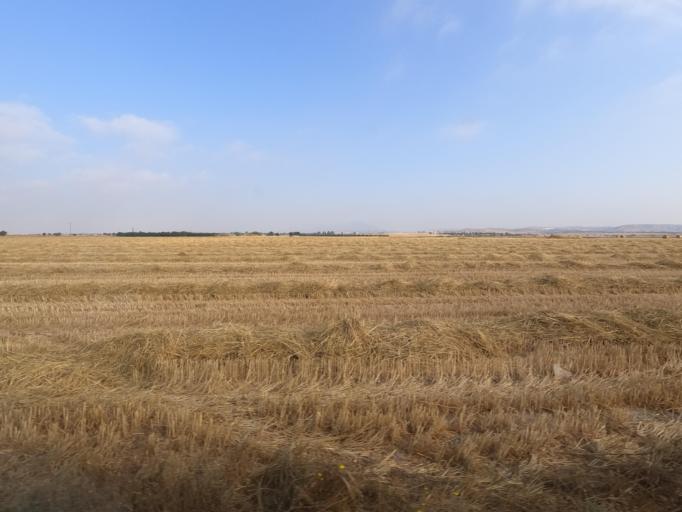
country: CY
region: Larnaka
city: Tersefanou
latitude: 34.8197
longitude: 33.5272
